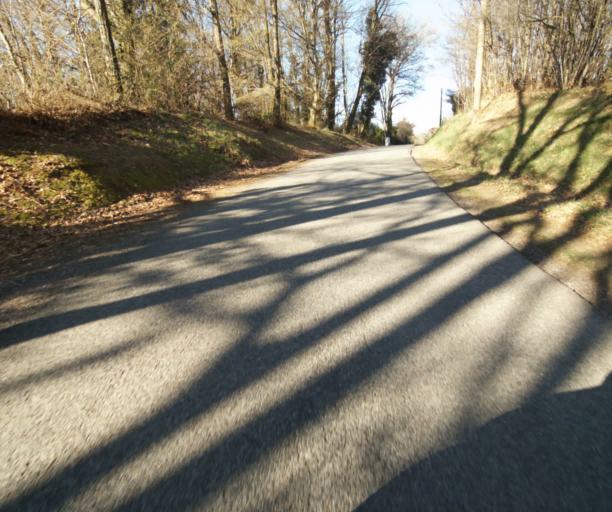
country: FR
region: Limousin
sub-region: Departement de la Correze
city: Saint-Clement
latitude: 45.3865
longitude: 1.6306
